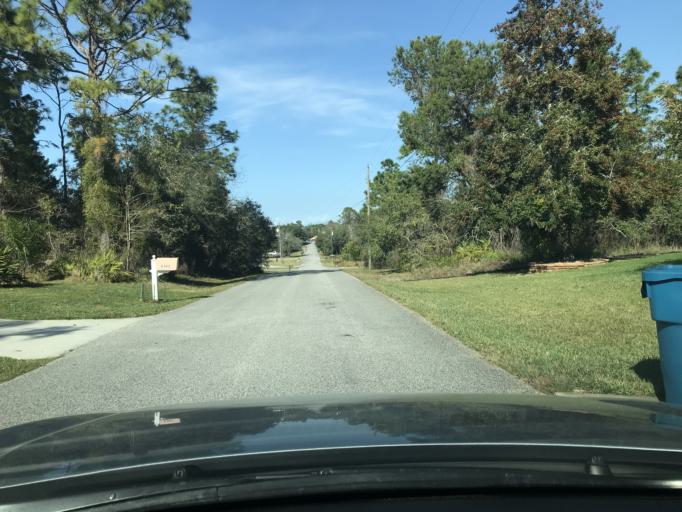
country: US
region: Florida
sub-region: Hernando County
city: North Weeki Wachee
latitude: 28.5499
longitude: -82.5462
